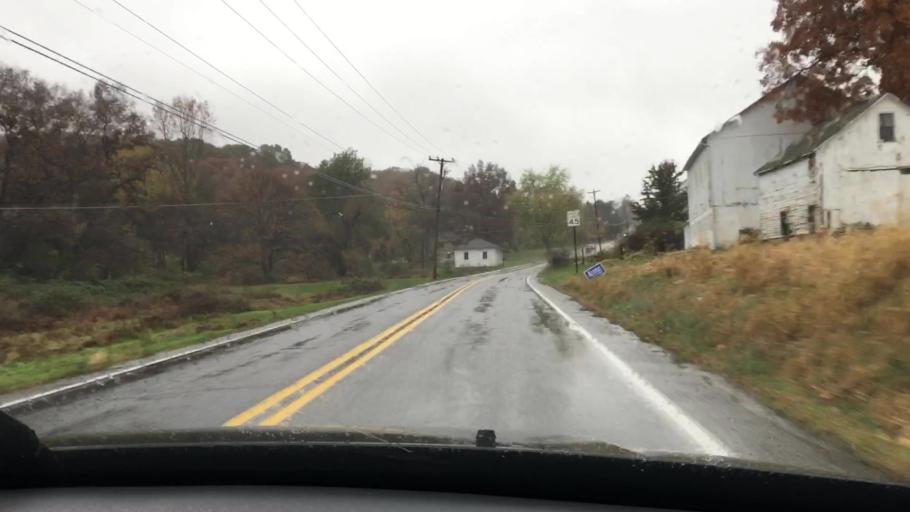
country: US
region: Pennsylvania
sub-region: York County
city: Glen Rock
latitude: 39.7665
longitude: -76.7615
